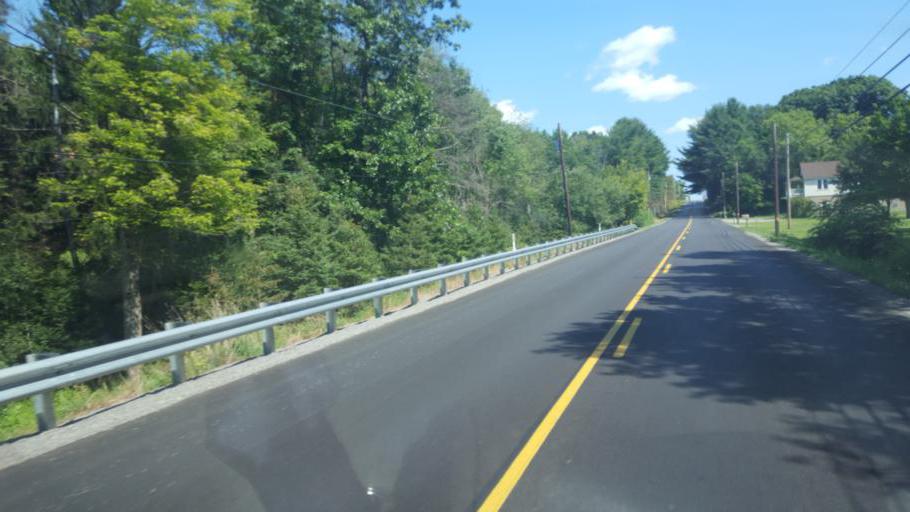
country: US
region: Pennsylvania
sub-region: Butler County
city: Chicora
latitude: 41.1015
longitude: -79.6717
